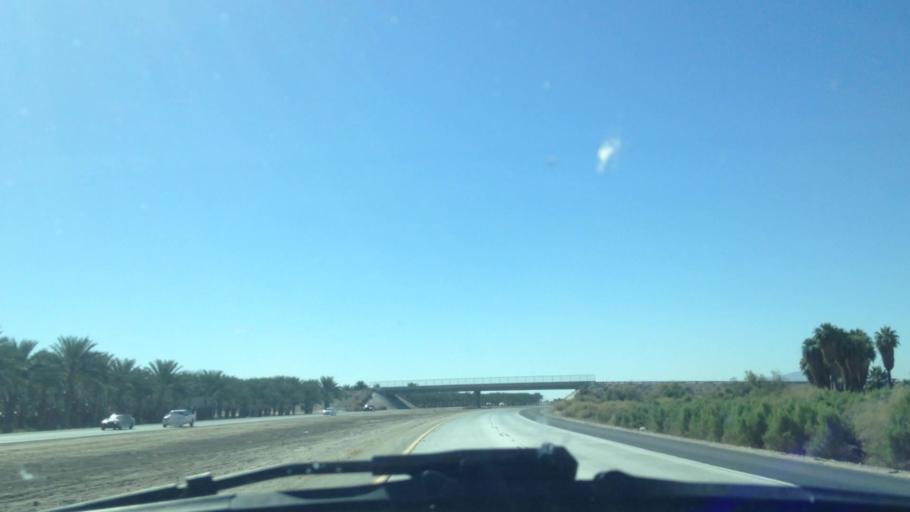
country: US
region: California
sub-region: Riverside County
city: Thermal
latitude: 33.6300
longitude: -116.1241
